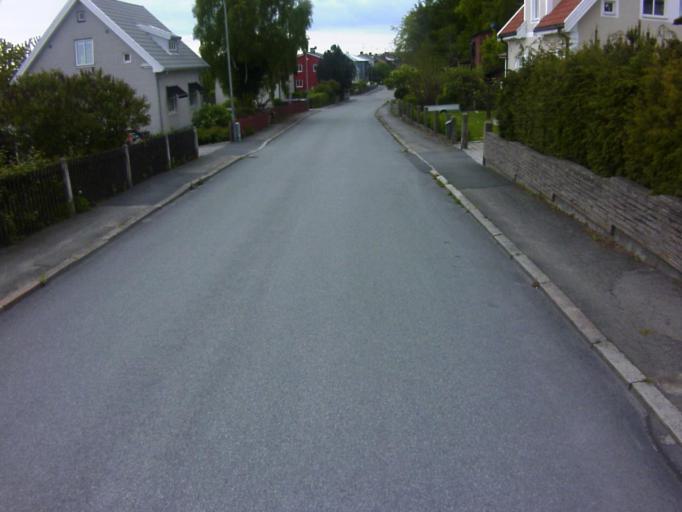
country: SE
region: Blekinge
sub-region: Solvesborgs Kommun
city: Soelvesborg
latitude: 56.0519
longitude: 14.5723
